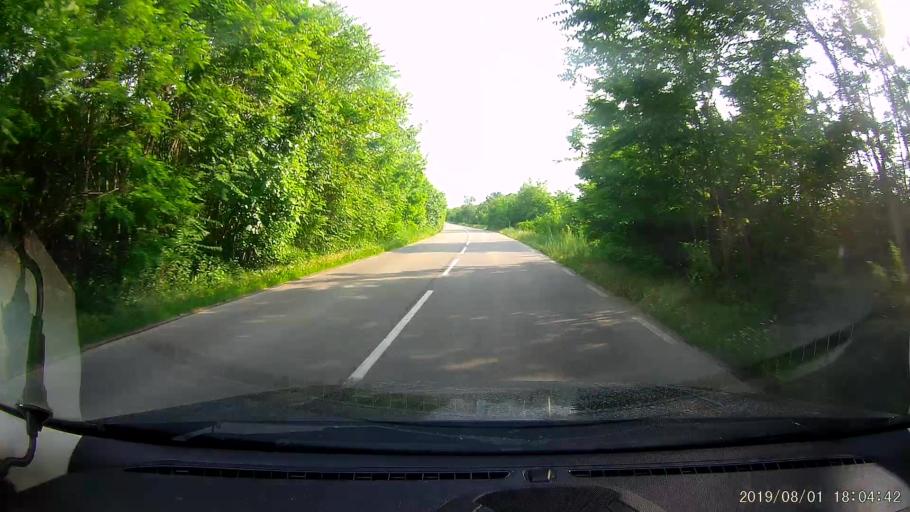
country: BG
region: Silistra
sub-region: Obshtina Alfatar
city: Alfatar
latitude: 43.9040
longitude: 27.2739
